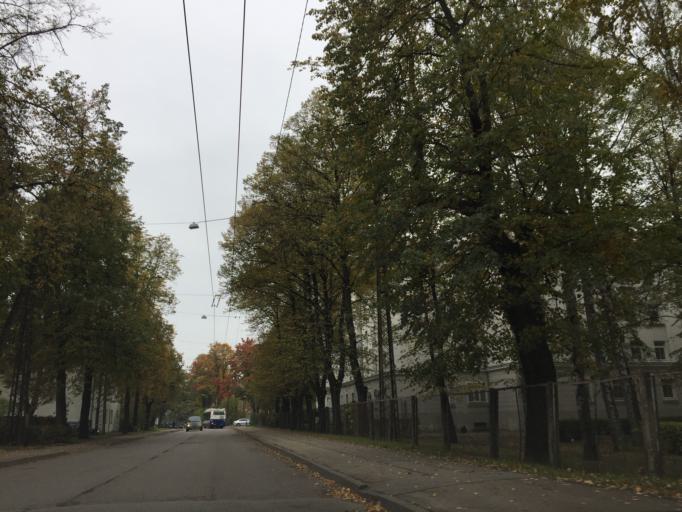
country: LV
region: Riga
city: Riga
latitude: 56.9173
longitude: 24.0916
